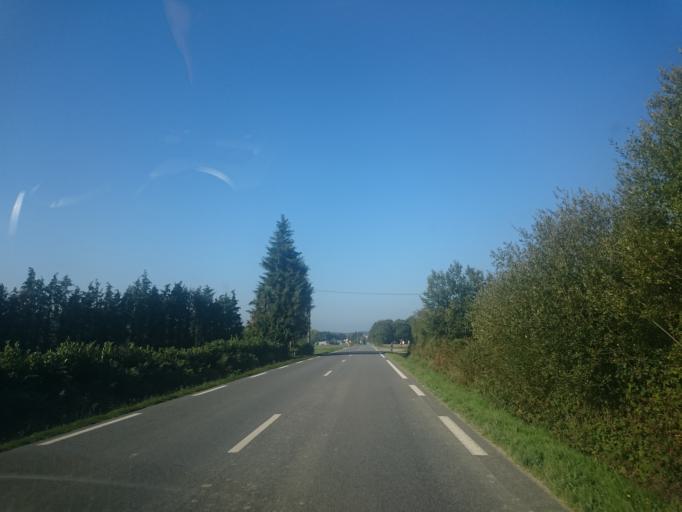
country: FR
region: Brittany
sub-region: Departement d'Ille-et-Vilaine
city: Tresboeuf
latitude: 47.9192
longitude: -1.5692
